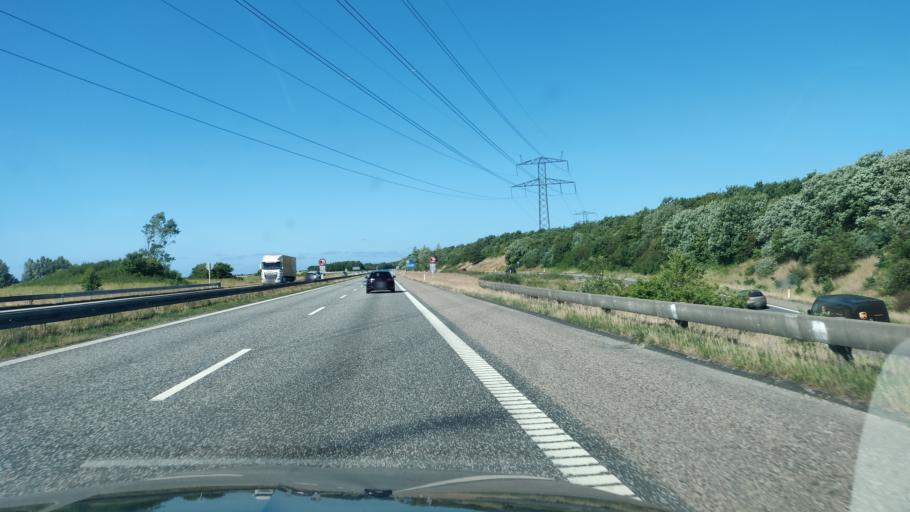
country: DK
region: North Denmark
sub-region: Rebild Kommune
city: Stovring
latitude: 56.8268
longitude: 9.7249
